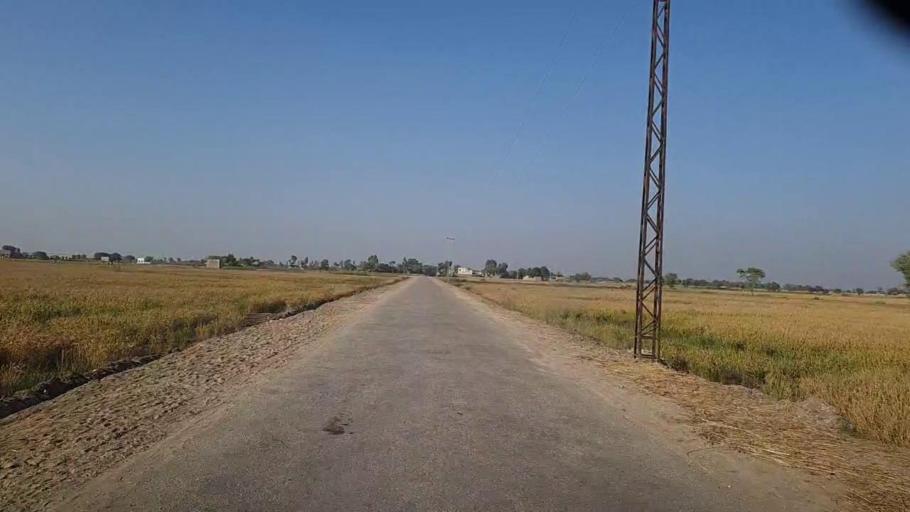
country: PK
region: Sindh
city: Tangwani
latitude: 28.2898
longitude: 68.9516
